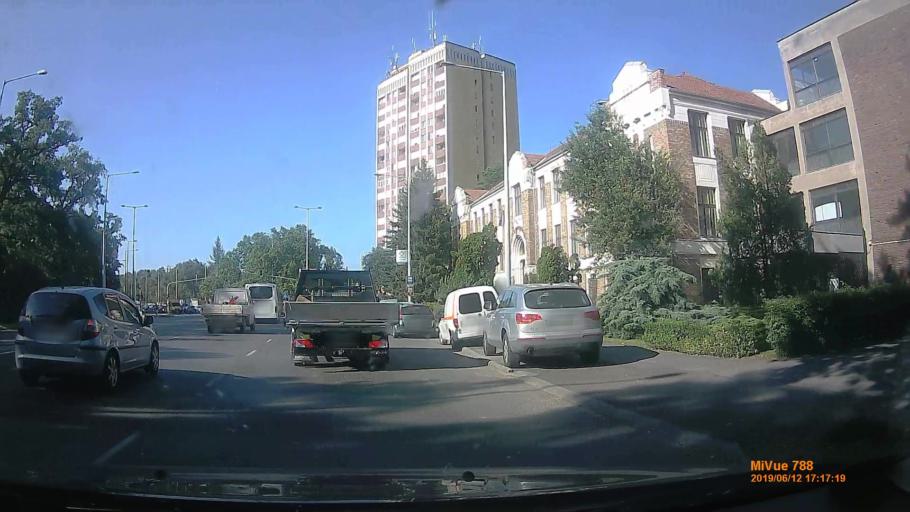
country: HU
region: Csongrad
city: Szeged
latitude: 46.2491
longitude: 20.1666
